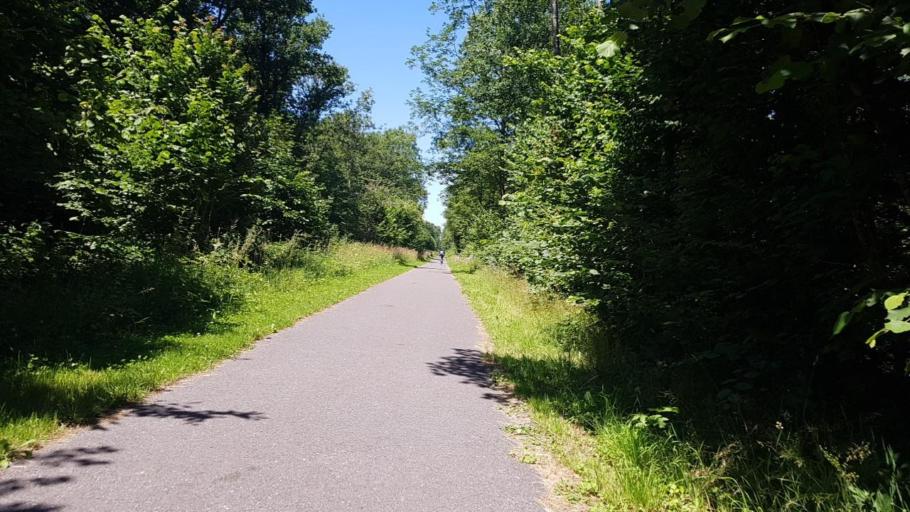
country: BE
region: Wallonia
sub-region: Province du Hainaut
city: Beaumont
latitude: 50.1688
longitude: 4.2414
